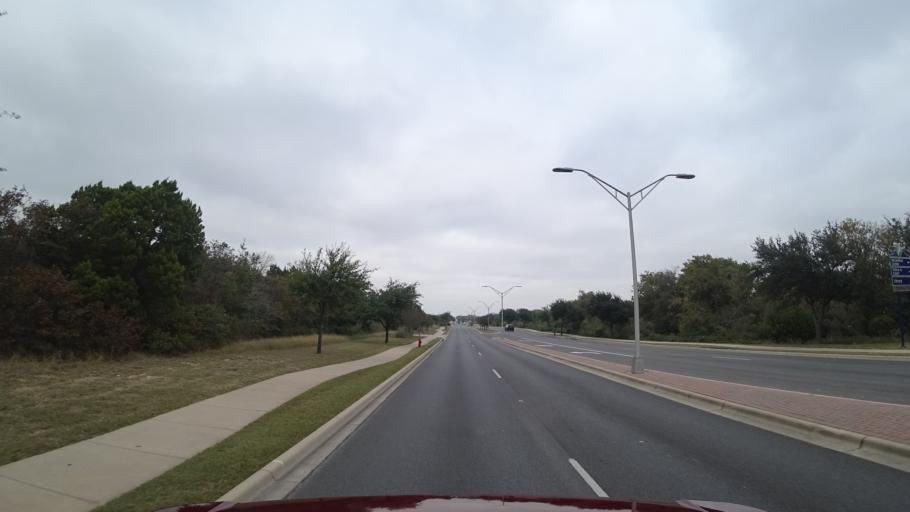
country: US
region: Texas
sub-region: Williamson County
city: Cedar Park
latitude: 30.5102
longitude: -97.8493
